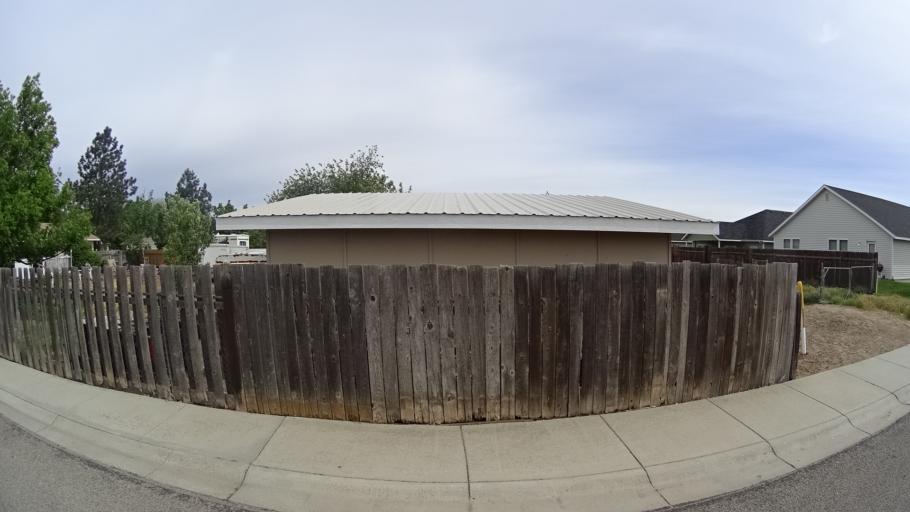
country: US
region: Idaho
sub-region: Ada County
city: Garden City
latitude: 43.5348
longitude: -116.3045
